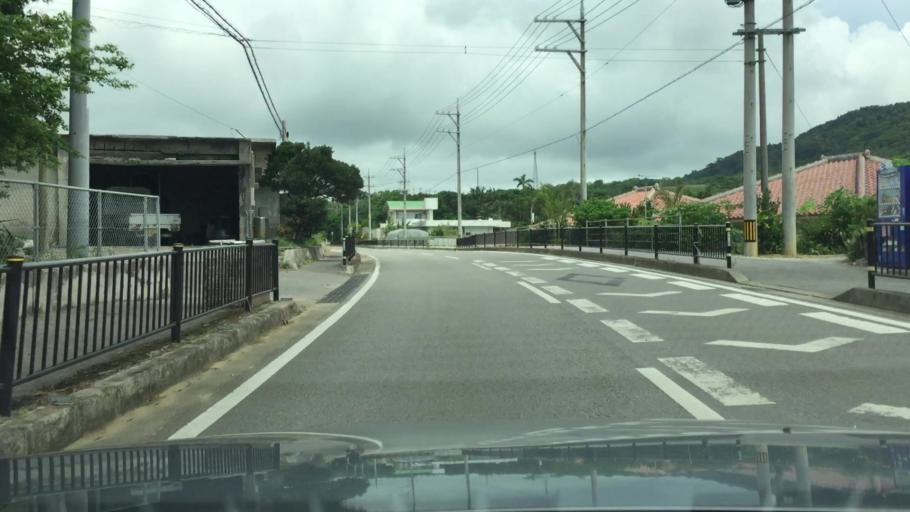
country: JP
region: Okinawa
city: Ishigaki
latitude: 24.3927
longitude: 124.1622
